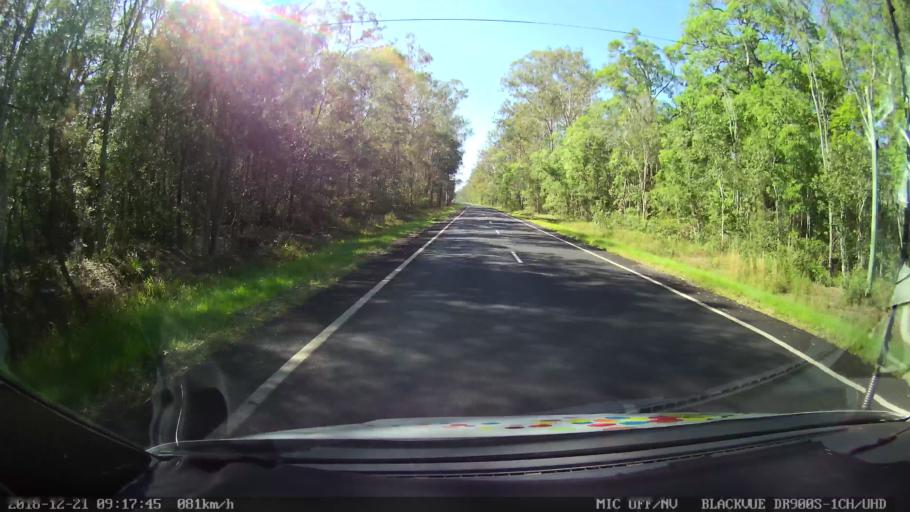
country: AU
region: New South Wales
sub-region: Clarence Valley
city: Maclean
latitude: -29.2959
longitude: 152.9917
